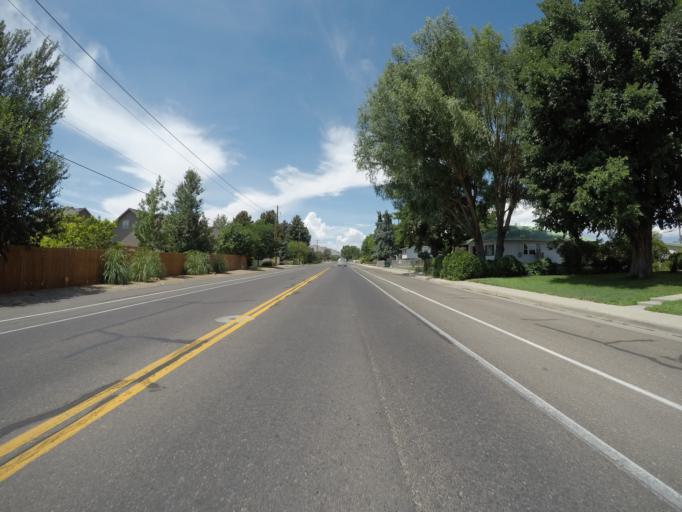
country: US
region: Utah
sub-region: Uintah County
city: Vernal
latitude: 40.4484
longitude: -109.5338
